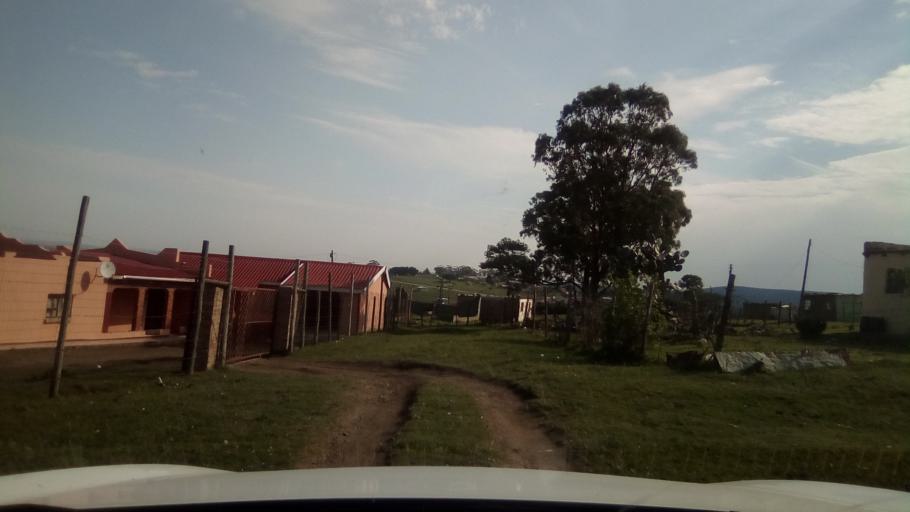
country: ZA
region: Eastern Cape
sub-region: Buffalo City Metropolitan Municipality
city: Bhisho
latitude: -32.9886
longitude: 27.2699
